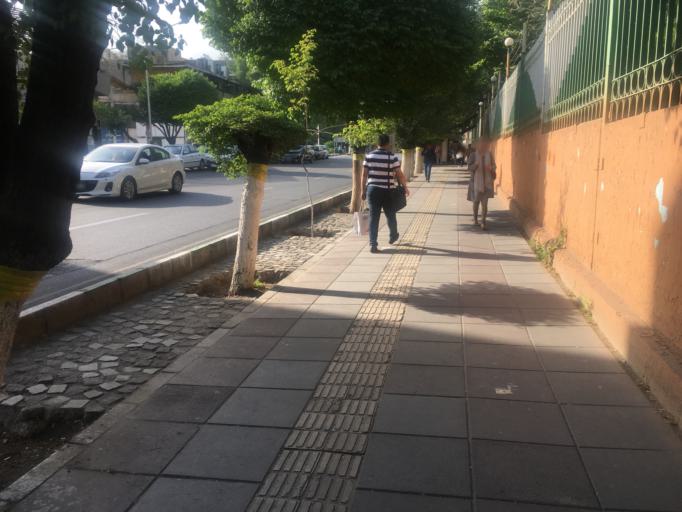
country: IR
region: Tehran
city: Tajrish
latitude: 35.7928
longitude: 51.4772
